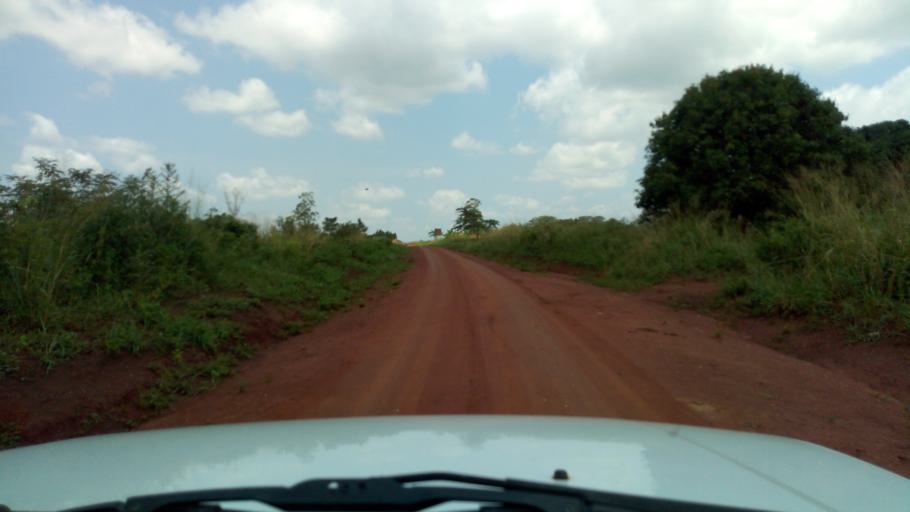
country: UG
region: Western Region
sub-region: Masindi District
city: Masindi
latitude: 1.7563
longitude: 31.8570
